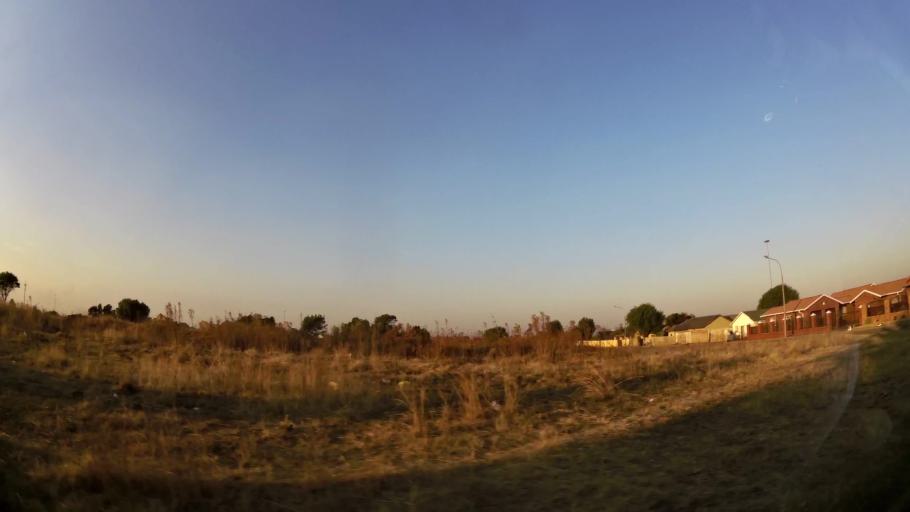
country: ZA
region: Gauteng
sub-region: West Rand District Municipality
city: Randfontein
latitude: -26.2090
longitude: 27.7031
